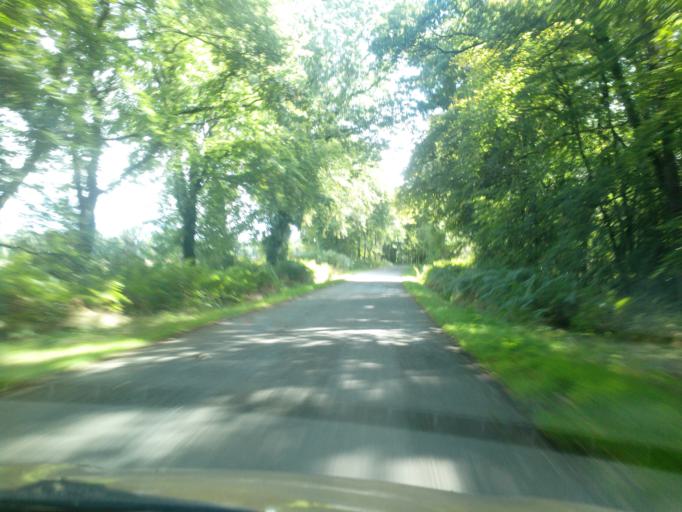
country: FR
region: Brittany
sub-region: Departement des Cotes-d'Armor
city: Merdrignac
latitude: 48.1292
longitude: -2.3889
